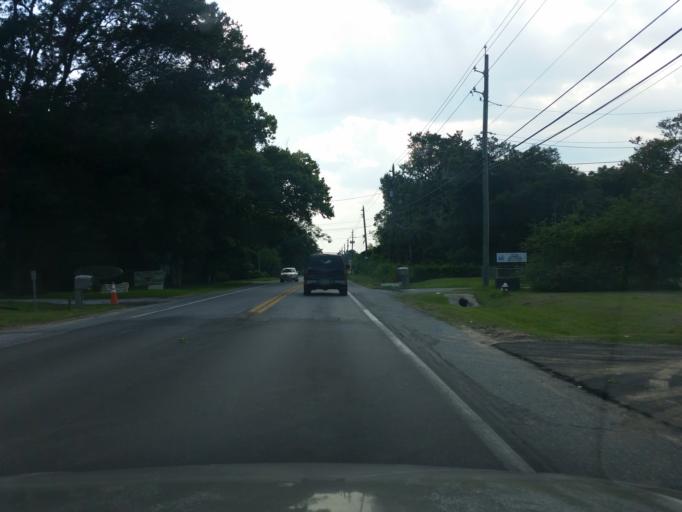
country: US
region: Florida
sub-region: Escambia County
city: Ferry Pass
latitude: 30.5108
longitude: -87.2305
